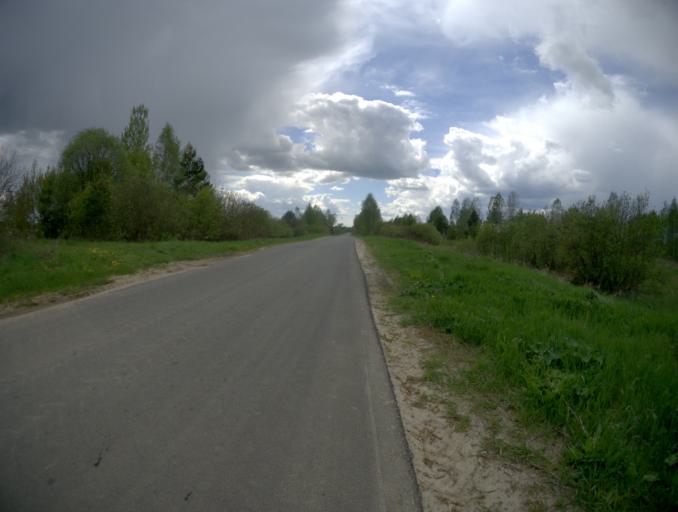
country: RU
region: Vladimir
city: Velikodvorskiy
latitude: 55.2623
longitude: 40.7890
